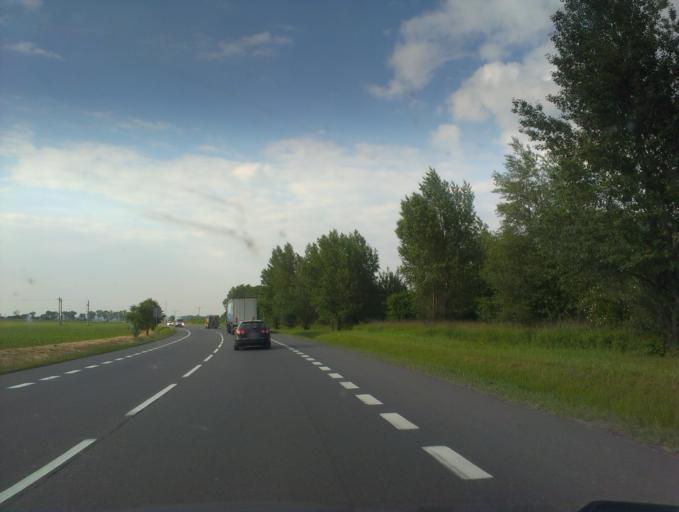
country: PL
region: Lower Silesian Voivodeship
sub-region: Powiat trzebnicki
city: Trzebnica
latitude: 51.3196
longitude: 17.0535
